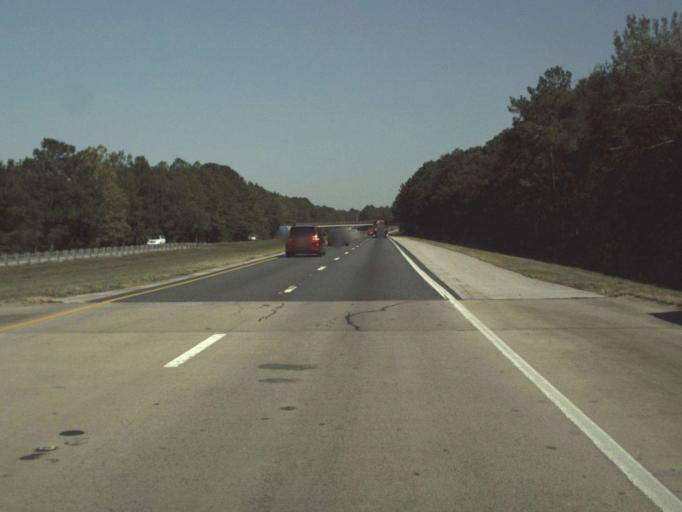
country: US
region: Florida
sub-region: Holmes County
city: Bonifay
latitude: 30.7593
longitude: -85.8042
